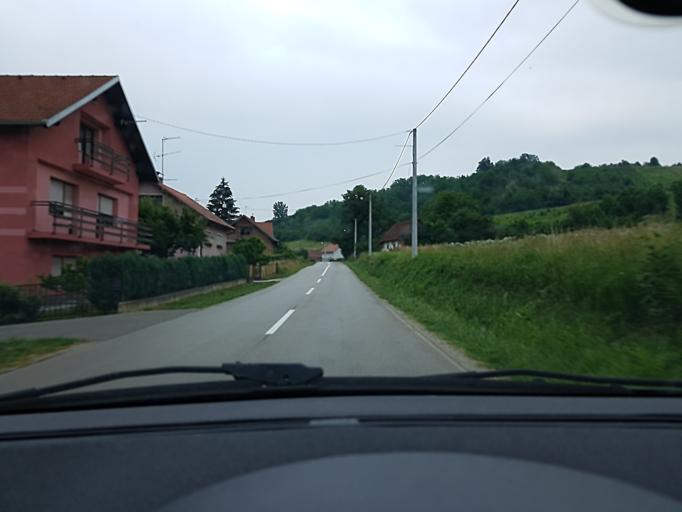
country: HR
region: Zagrebacka
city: Jakovlje
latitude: 45.9697
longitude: 15.8313
